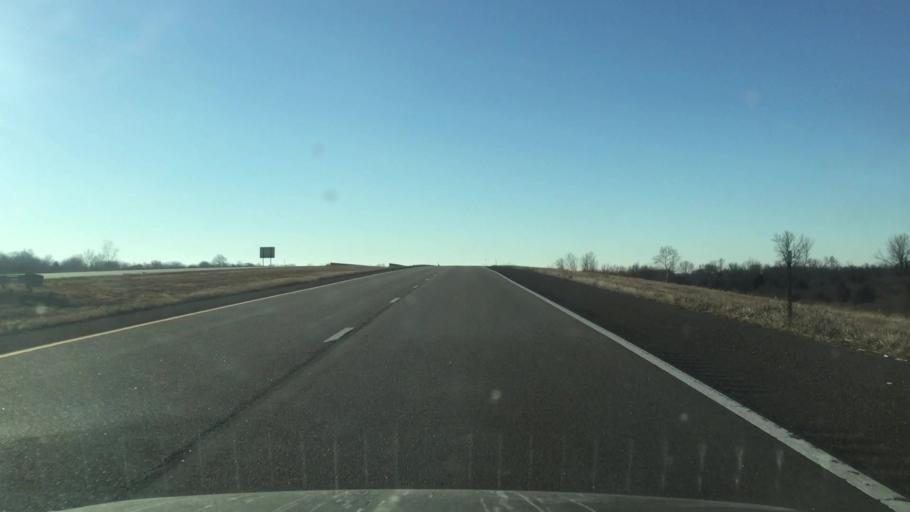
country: US
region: Kansas
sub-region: Miami County
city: Paola
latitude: 38.6351
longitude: -94.8360
